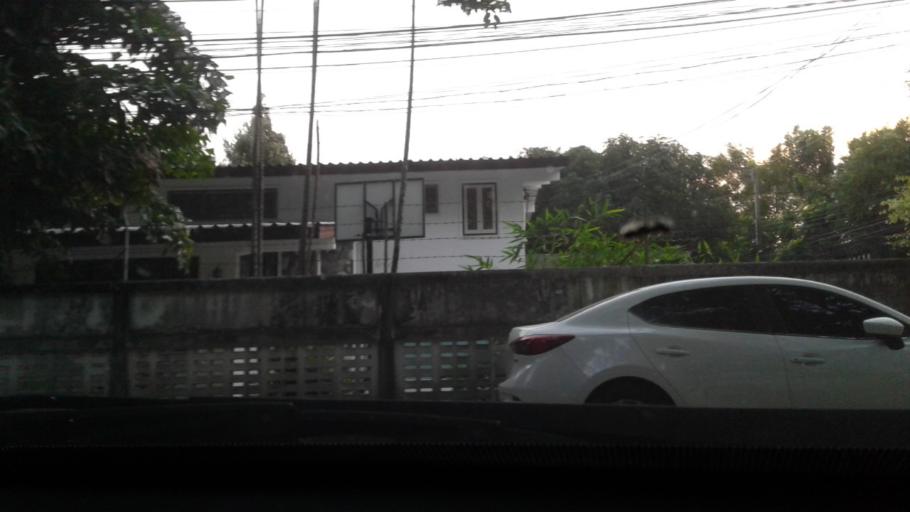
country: TH
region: Bangkok
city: Phaya Thai
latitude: 13.7763
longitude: 100.5410
